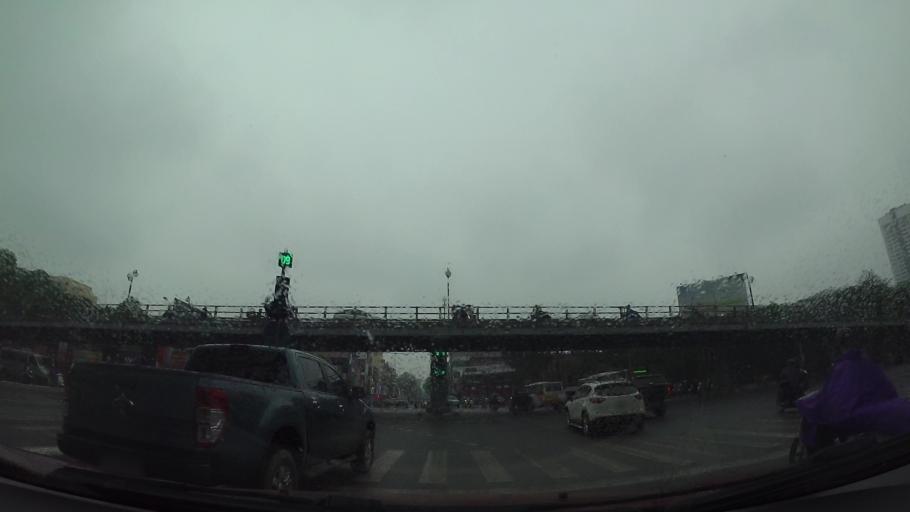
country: VN
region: Ha Noi
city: Dong Da
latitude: 21.0094
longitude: 105.8242
